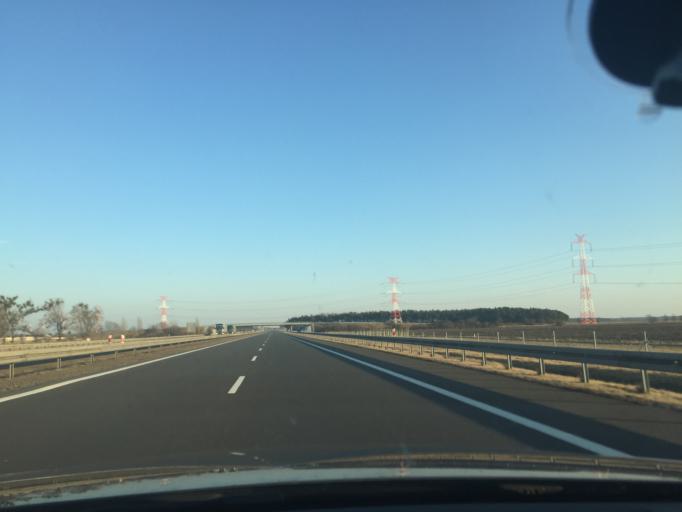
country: PL
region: Greater Poland Voivodeship
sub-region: Powiat wrzesinski
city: Kolaczkowo
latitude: 52.2847
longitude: 17.6828
